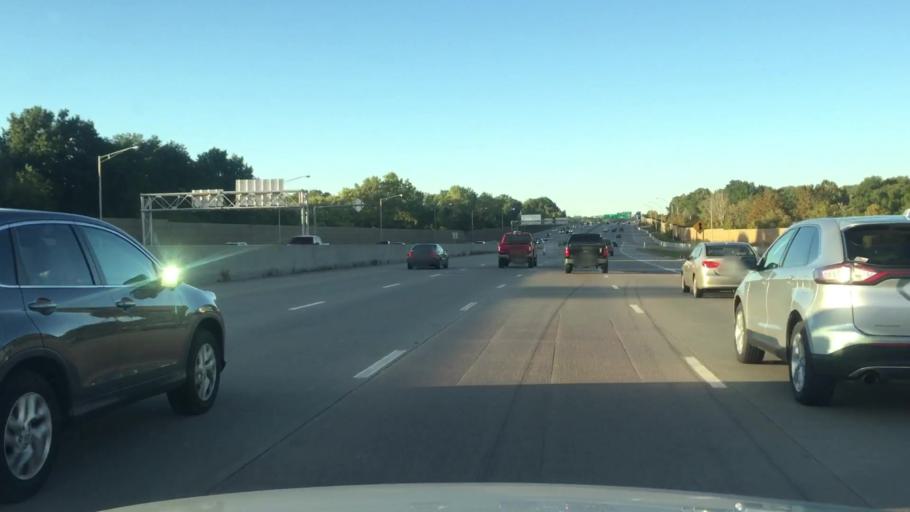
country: US
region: Kansas
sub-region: Johnson County
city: Lenexa
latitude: 38.9439
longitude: -94.7052
